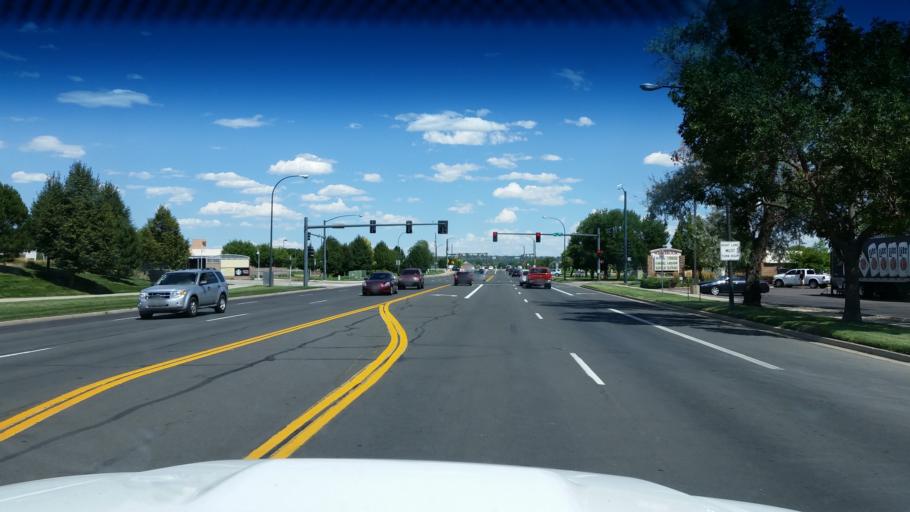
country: US
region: Colorado
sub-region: Broomfield County
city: Broomfield
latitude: 39.8781
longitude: -105.0996
